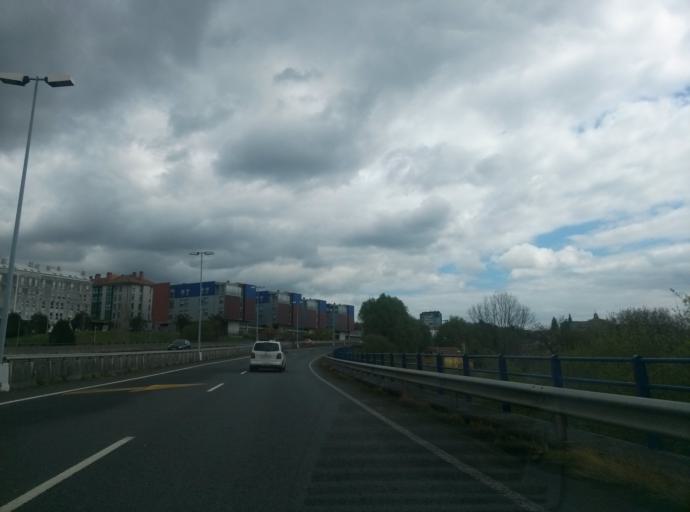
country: ES
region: Galicia
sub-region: Provincia da Coruna
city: Santiago de Compostela
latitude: 42.8640
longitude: -8.5629
